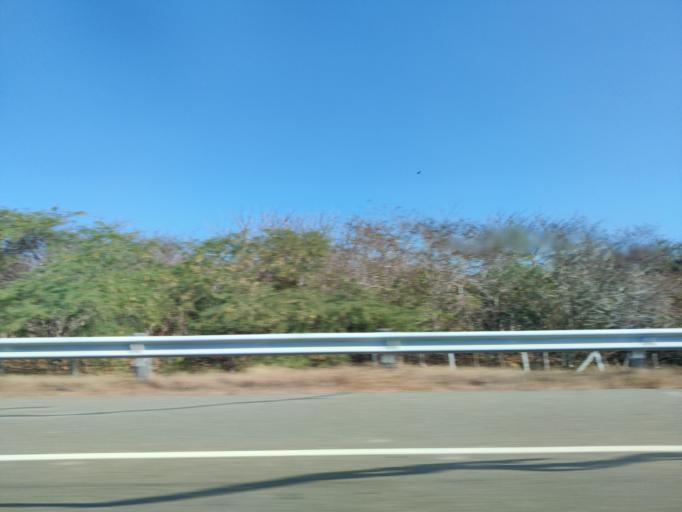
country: CO
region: Atlantico
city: Puerto Colombia
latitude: 10.9686
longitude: -74.9868
